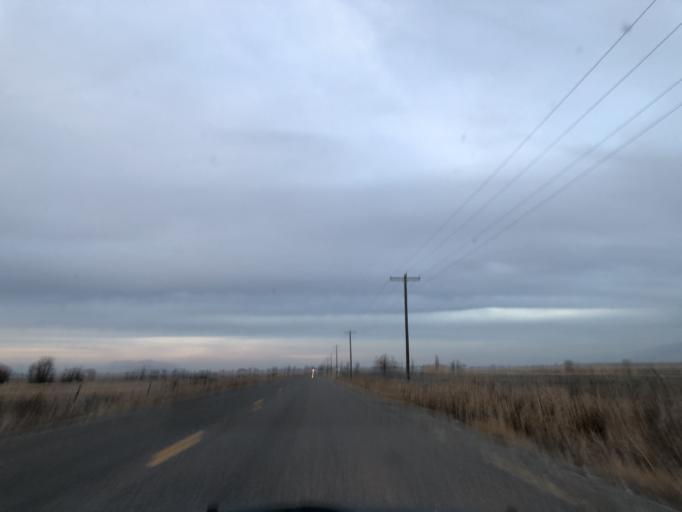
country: US
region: Utah
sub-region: Cache County
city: Benson
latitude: 41.7679
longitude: -111.9117
